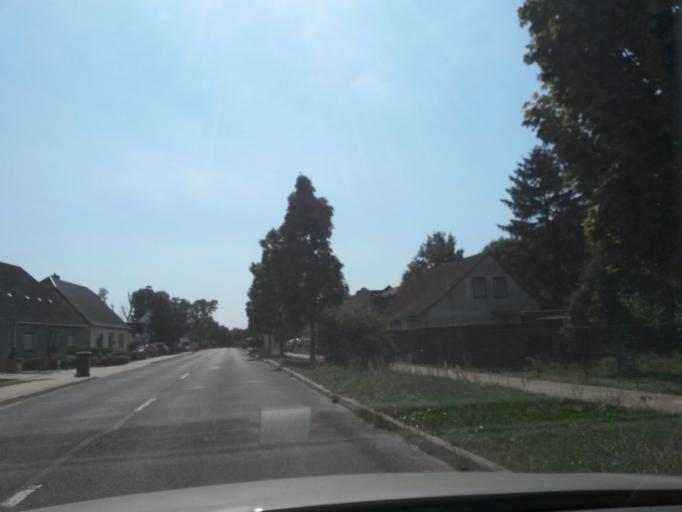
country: DE
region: Saxony-Anhalt
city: Jerichow
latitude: 52.3934
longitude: 11.9941
